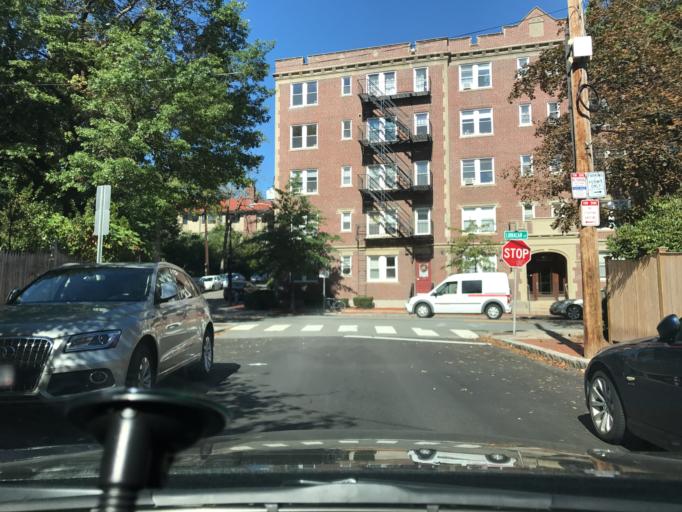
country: US
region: Massachusetts
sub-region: Middlesex County
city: Cambridge
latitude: 42.3842
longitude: -71.1211
